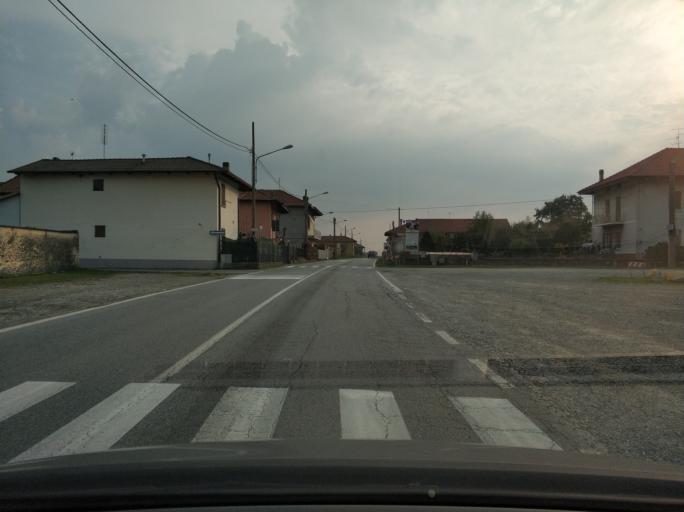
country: IT
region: Piedmont
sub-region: Provincia di Torino
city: San Francesco al Campo
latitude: 45.2377
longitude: 7.6531
